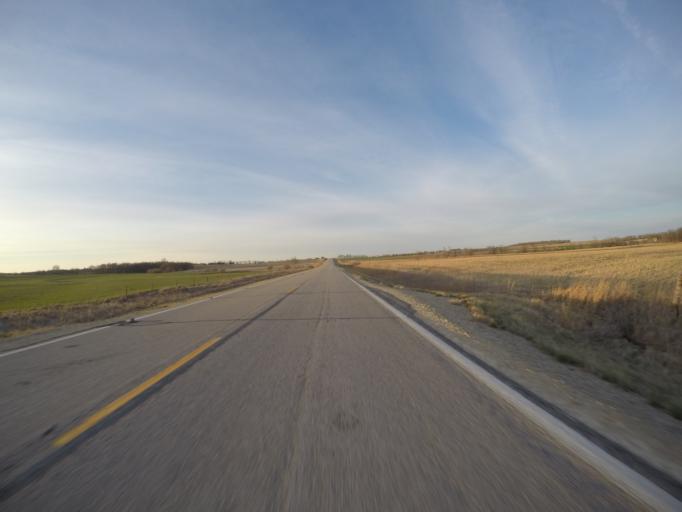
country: US
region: Kansas
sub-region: Clay County
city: Clay Center
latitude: 39.4007
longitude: -96.8490
